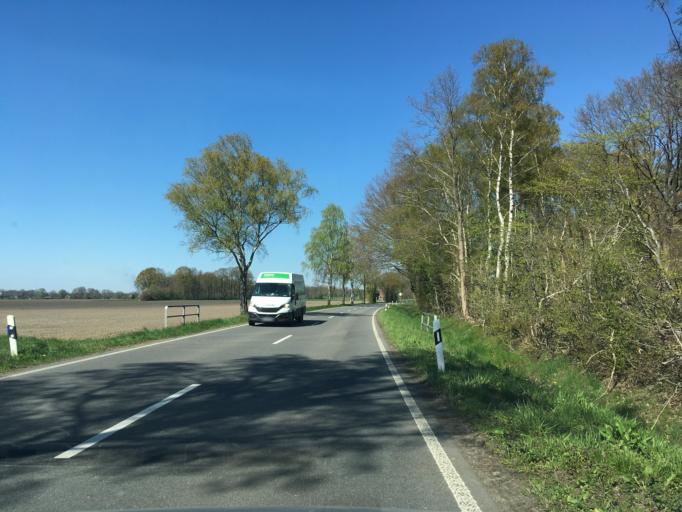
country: DE
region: North Rhine-Westphalia
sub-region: Regierungsbezirk Munster
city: Borken
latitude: 51.8627
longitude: 6.7902
